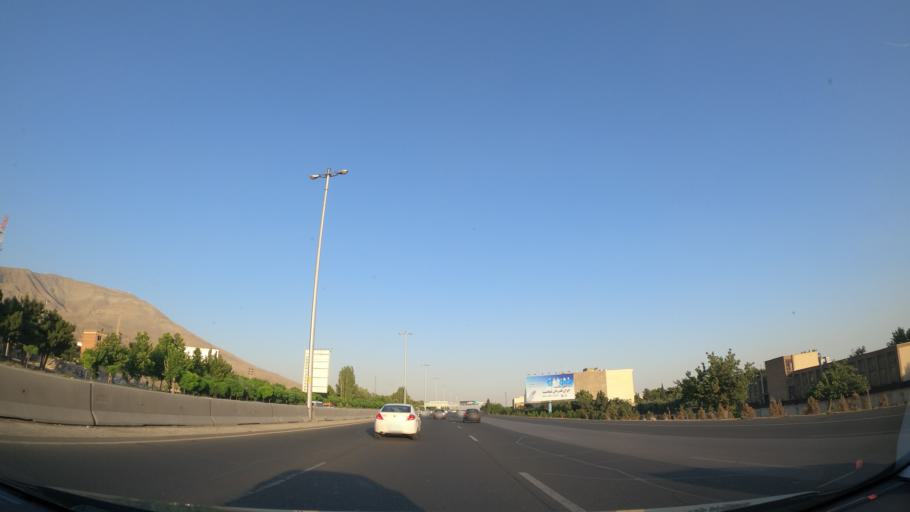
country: IR
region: Alborz
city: Karaj
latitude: 35.7849
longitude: 51.0276
